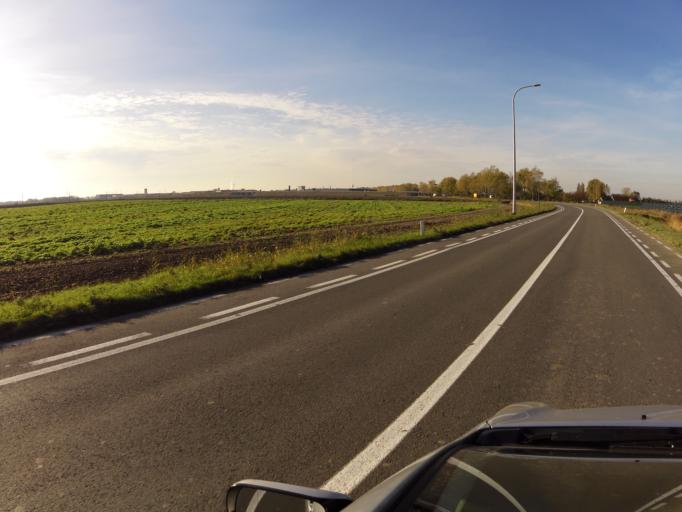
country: BE
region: Flanders
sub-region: Provincie West-Vlaanderen
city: Veurne
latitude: 51.0704
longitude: 2.7092
